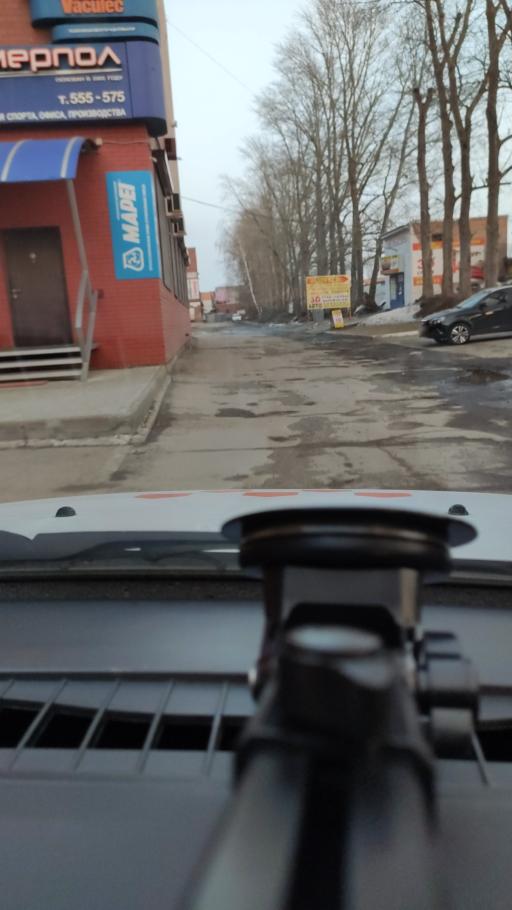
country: RU
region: Samara
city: Tol'yatti
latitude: 53.5402
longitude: 49.3028
